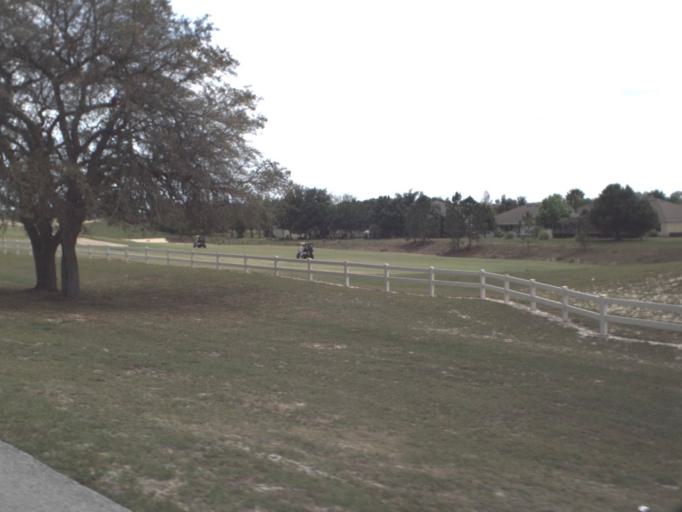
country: US
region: Florida
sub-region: Lake County
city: Mount Plymouth
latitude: 28.8512
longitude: -81.5662
